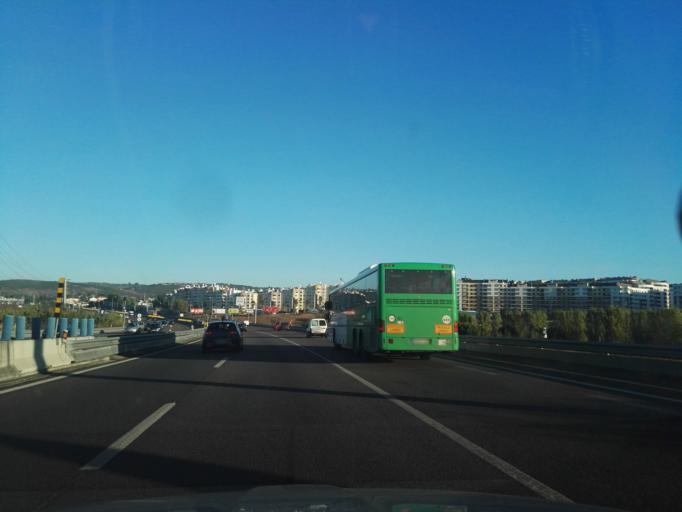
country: PT
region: Lisbon
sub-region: Loures
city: Loures
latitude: 38.8340
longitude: -9.1591
